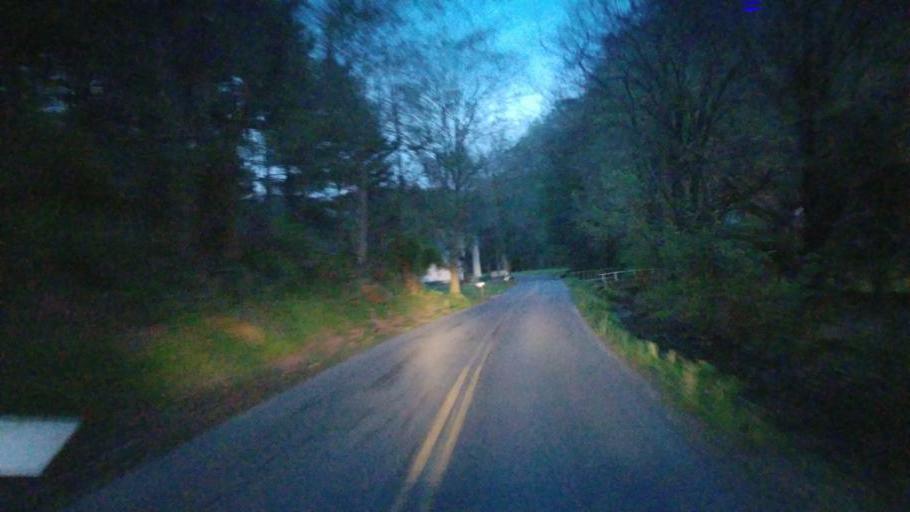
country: US
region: Virginia
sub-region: Smyth County
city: Atkins
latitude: 36.8403
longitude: -81.4574
